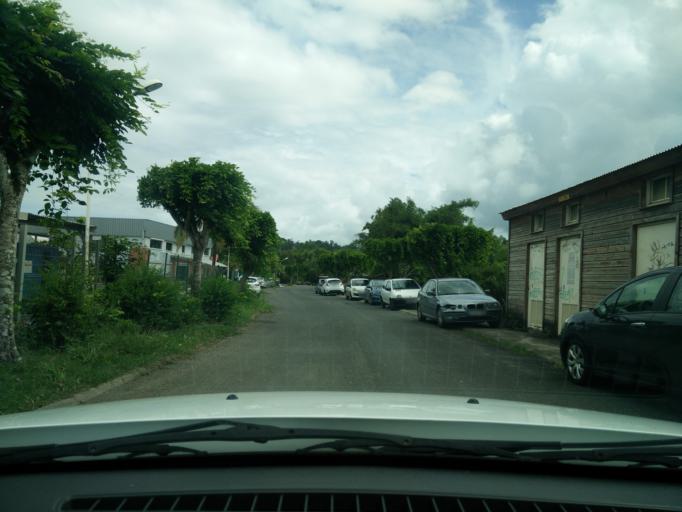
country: GP
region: Guadeloupe
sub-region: Guadeloupe
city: Petit-Bourg
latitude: 16.2017
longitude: -61.6089
